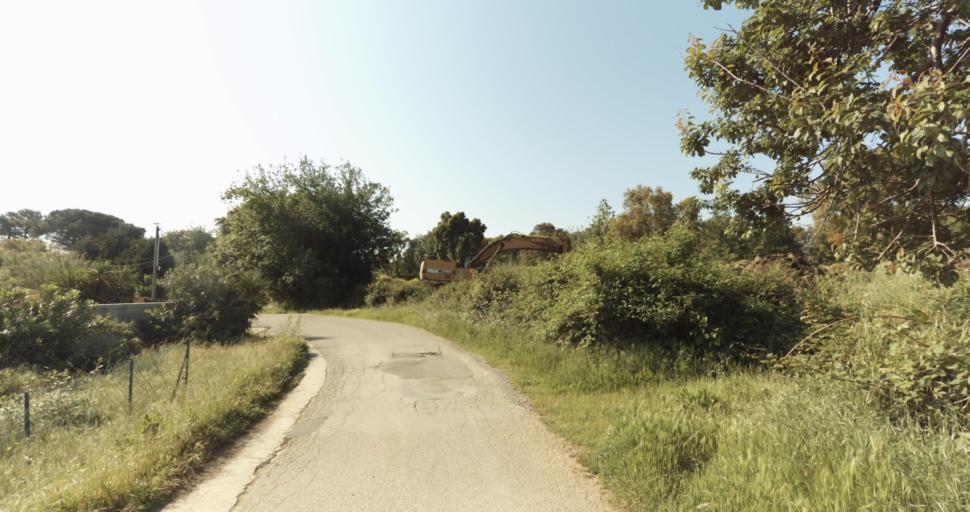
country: FR
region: Corsica
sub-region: Departement de la Haute-Corse
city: Biguglia
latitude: 42.6338
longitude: 9.4277
